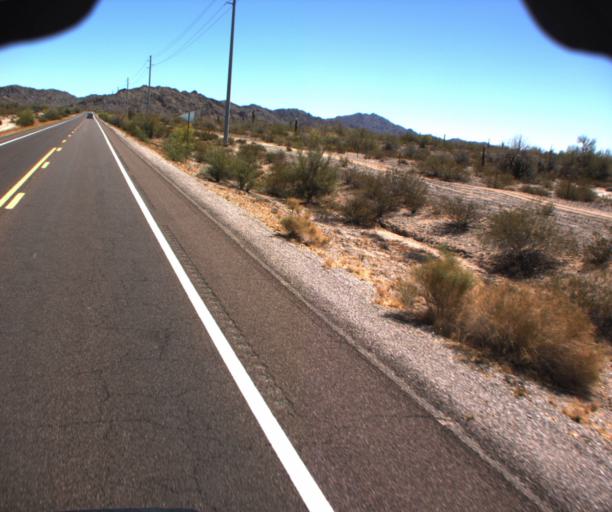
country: US
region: Arizona
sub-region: La Paz County
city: Salome
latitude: 33.7237
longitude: -113.6996
